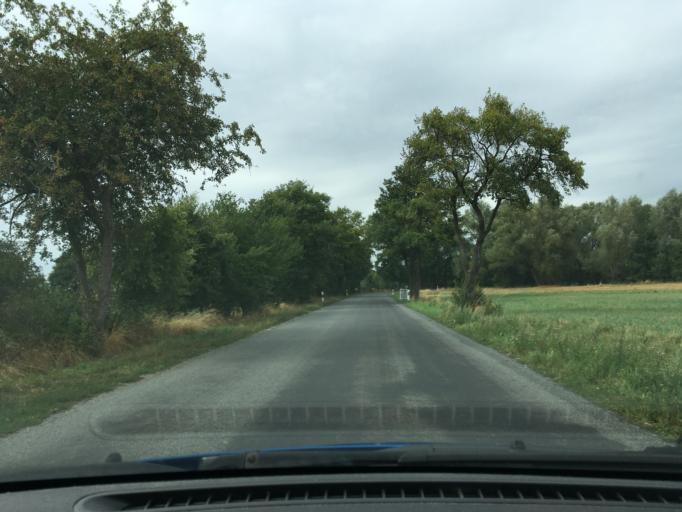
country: DE
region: Mecklenburg-Vorpommern
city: Stralendorf
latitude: 53.5400
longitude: 11.2897
